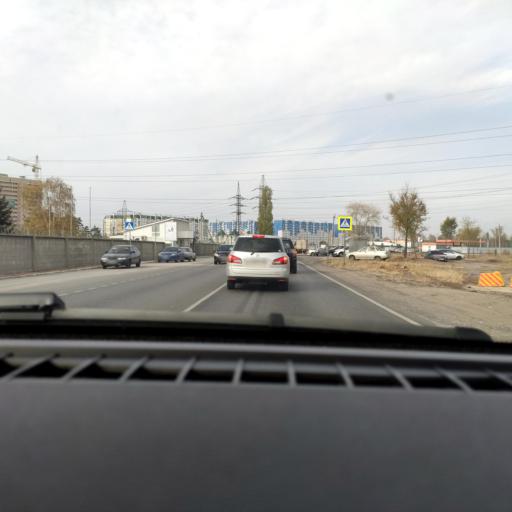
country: RU
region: Voronezj
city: Maslovka
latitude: 51.5886
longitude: 39.2524
